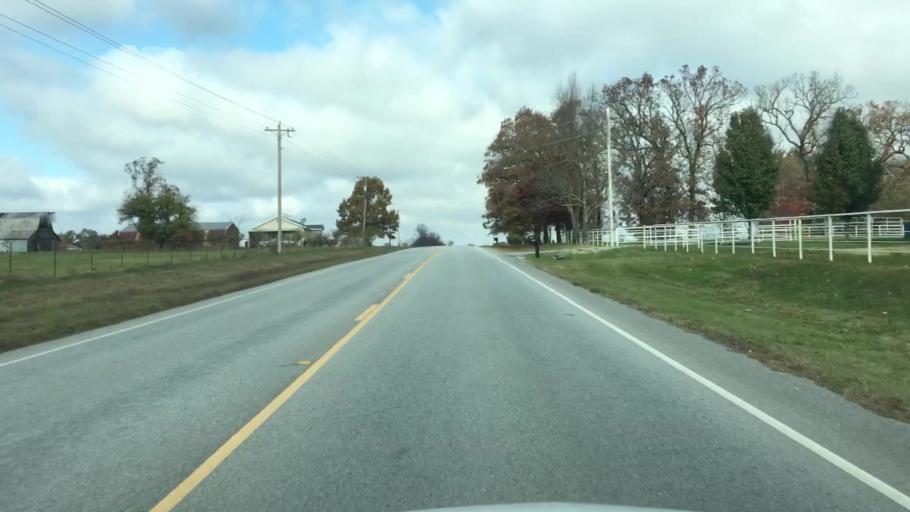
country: US
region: Arkansas
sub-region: Benton County
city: Centerton
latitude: 36.2678
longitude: -94.3503
